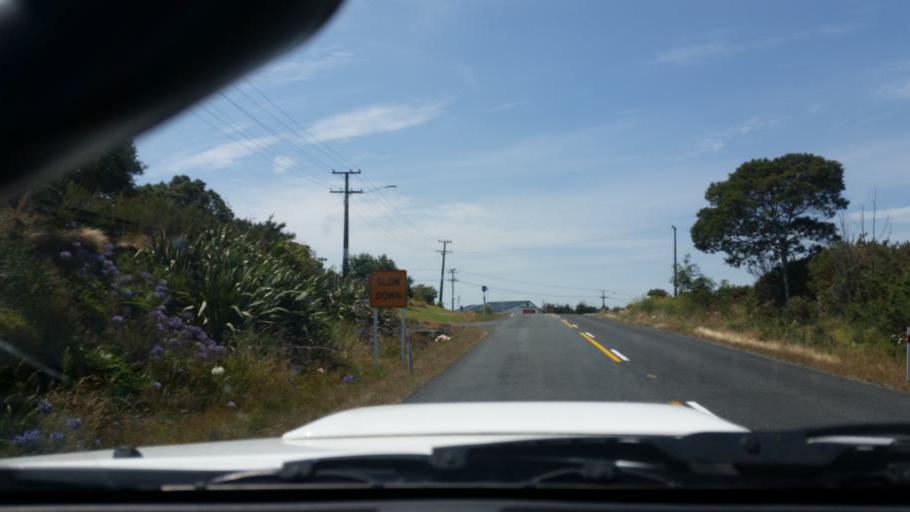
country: NZ
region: Northland
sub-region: Kaipara District
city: Dargaville
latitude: -36.0332
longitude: 173.9212
